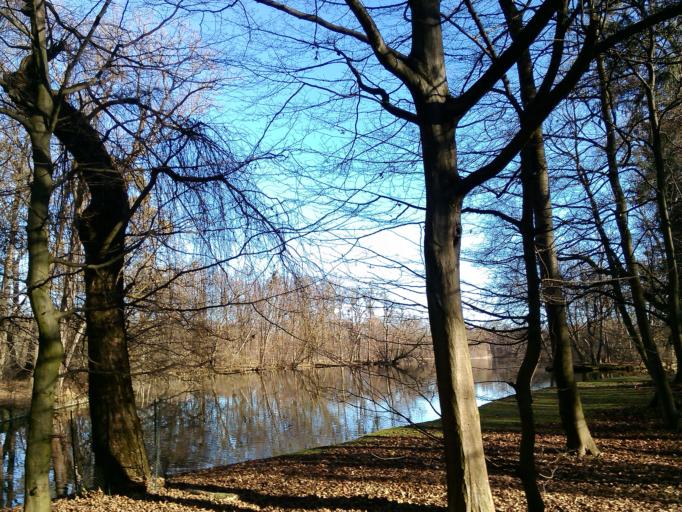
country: DE
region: Bavaria
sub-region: Upper Bavaria
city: Pasing
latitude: 48.1546
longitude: 11.4883
